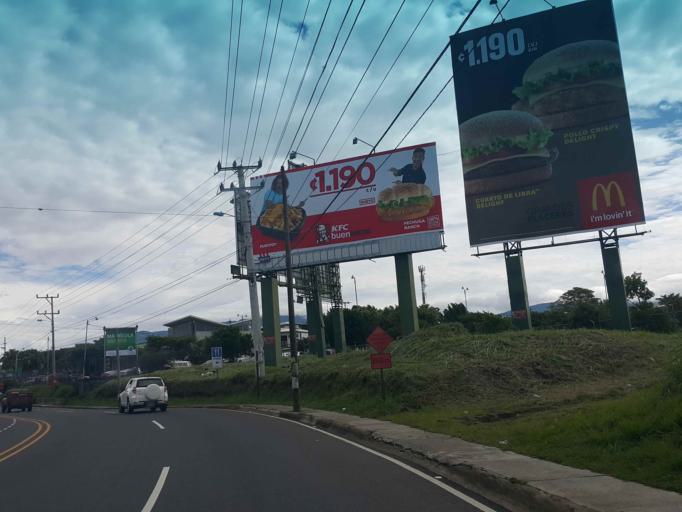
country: CR
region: Heredia
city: San Pablo
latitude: 9.9836
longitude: -84.1089
